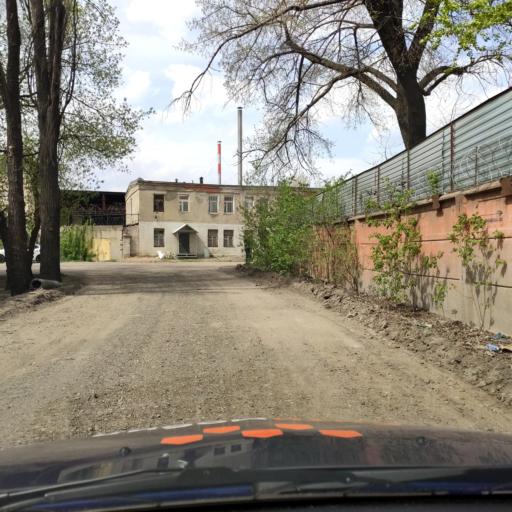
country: RU
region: Voronezj
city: Voronezh
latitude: 51.6726
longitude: 39.1716
